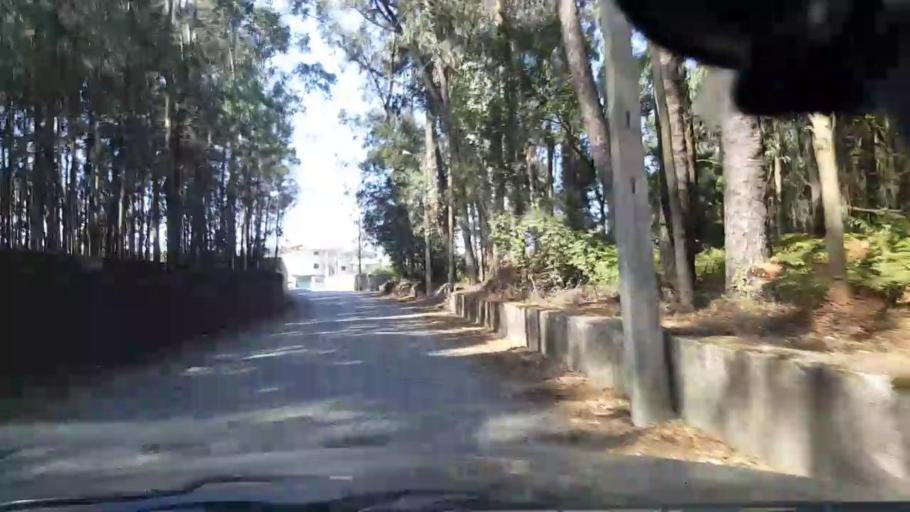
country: PT
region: Porto
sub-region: Povoa de Varzim
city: Pedroso
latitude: 41.3933
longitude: -8.7140
